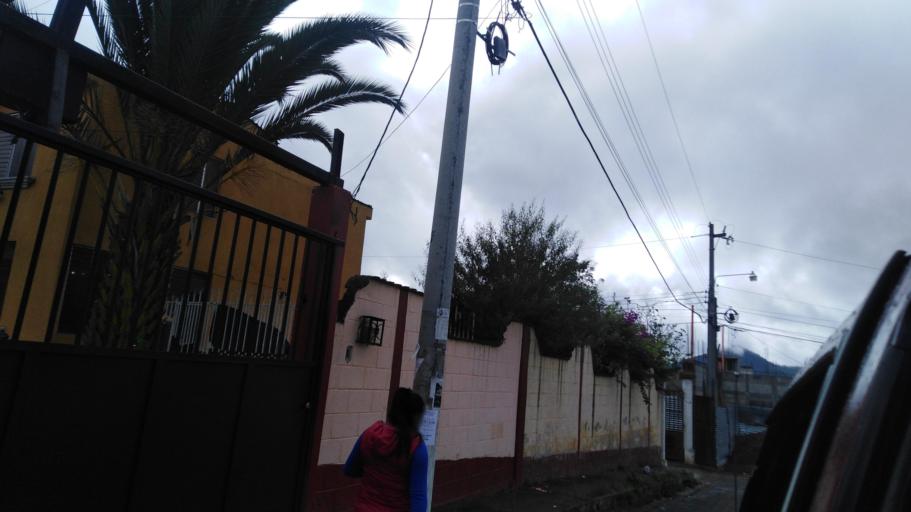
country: GT
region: Quetzaltenango
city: Quetzaltenango
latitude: 14.8535
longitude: -91.5064
